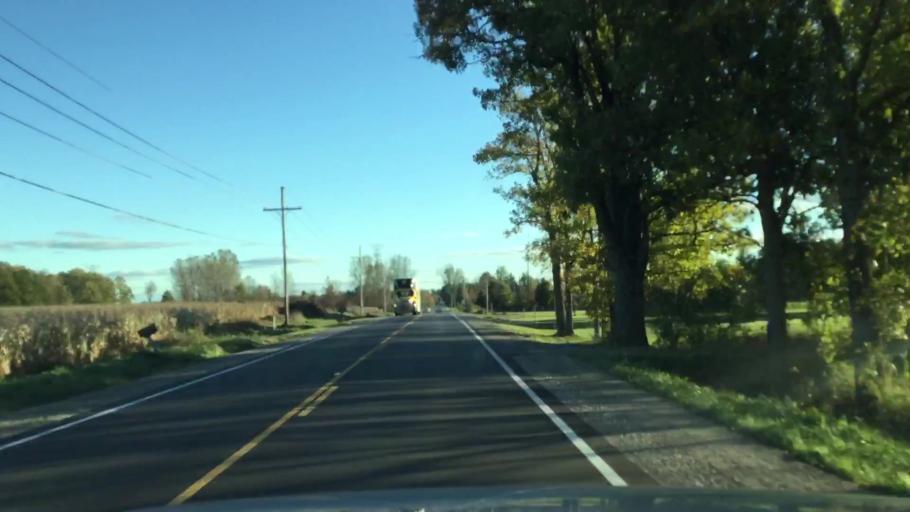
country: US
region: Michigan
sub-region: Lapeer County
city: Almont
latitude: 42.9428
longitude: -83.1448
